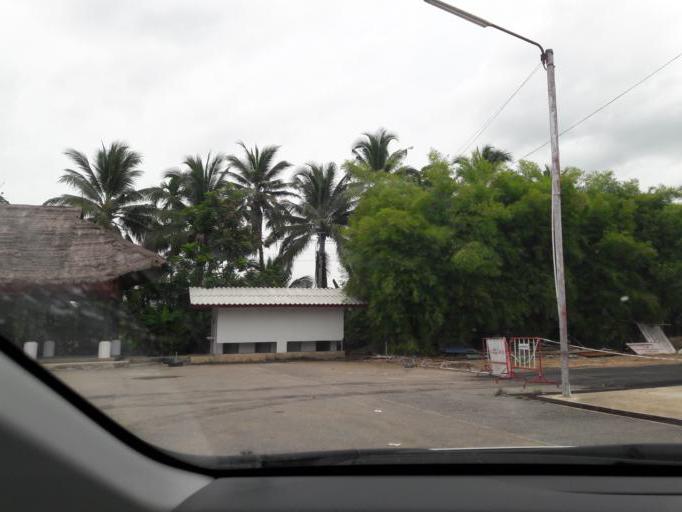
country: TH
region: Samut Sakhon
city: Ban Phaeo
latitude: 13.6025
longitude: 100.0244
